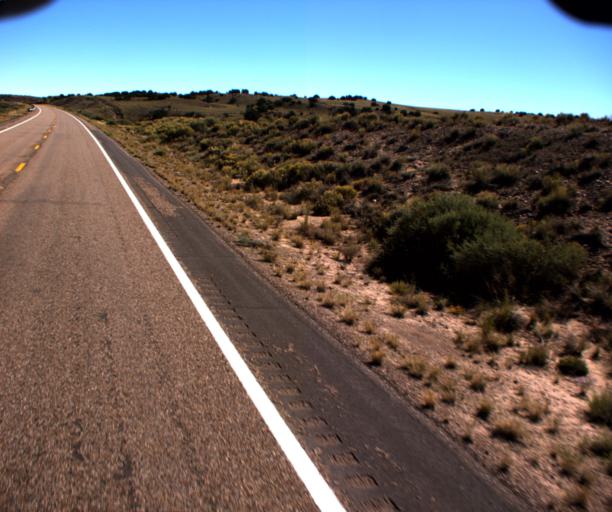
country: US
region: Arizona
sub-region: Apache County
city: Saint Johns
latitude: 34.5851
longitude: -109.5664
